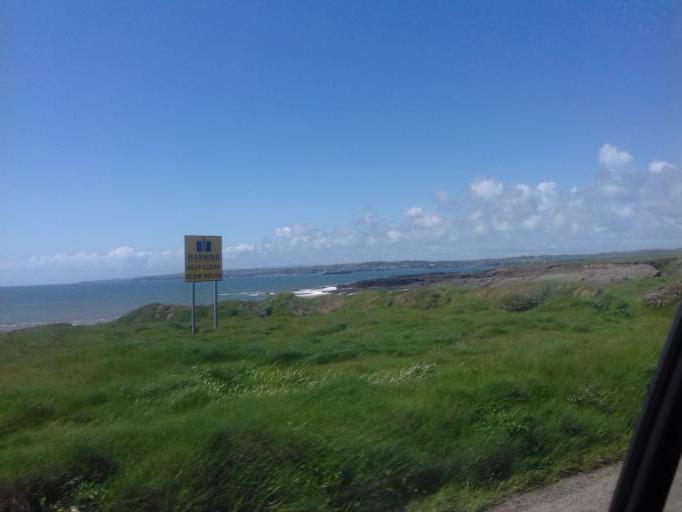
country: IE
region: Munster
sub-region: Waterford
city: Dunmore East
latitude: 52.1287
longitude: -6.9296
